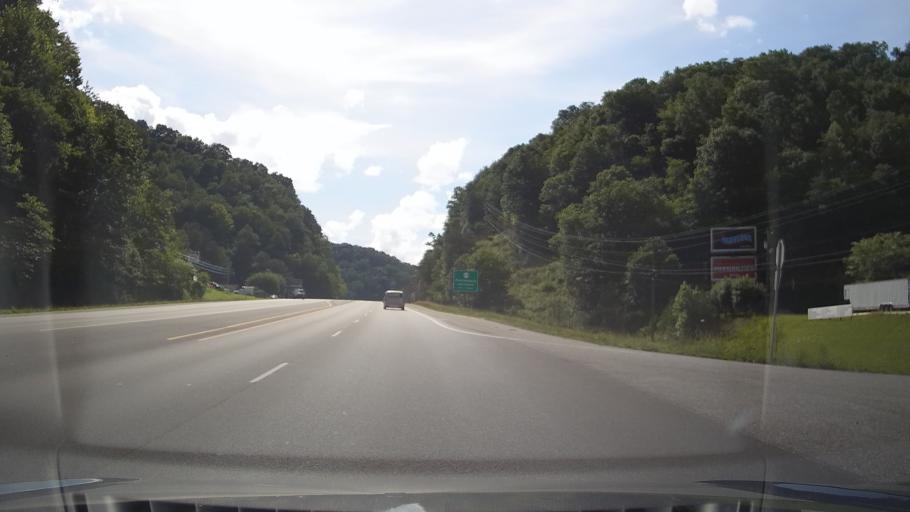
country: US
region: Kentucky
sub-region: Floyd County
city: Prestonsburg
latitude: 37.6435
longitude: -82.7683
